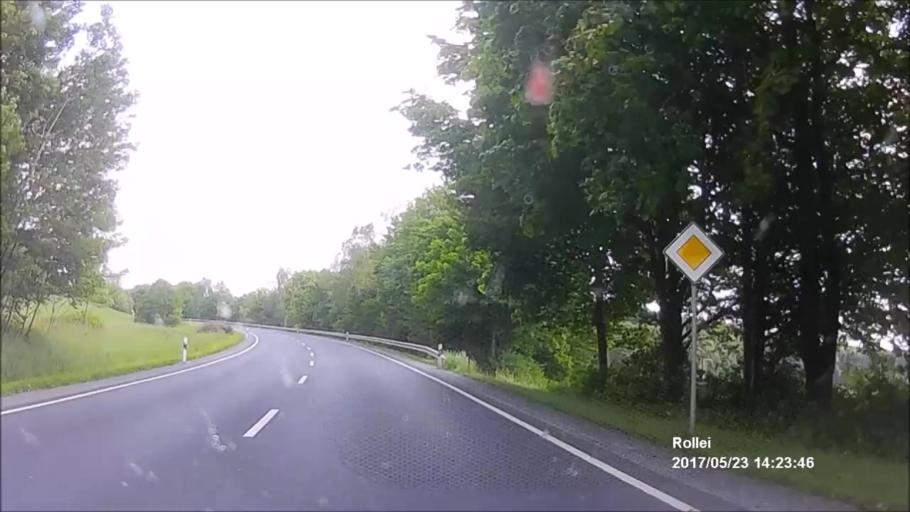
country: DE
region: Bavaria
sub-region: Upper Bavaria
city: Babensham
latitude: 48.0411
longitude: 12.2951
